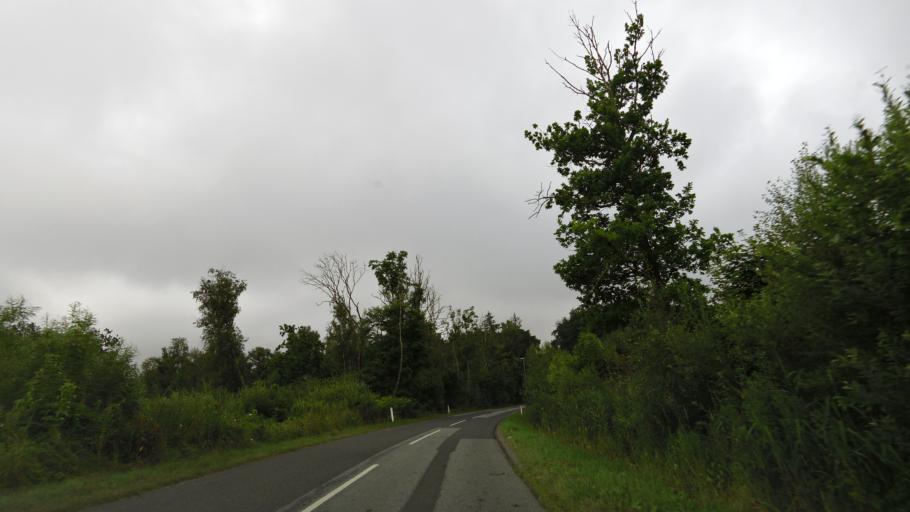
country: DK
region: South Denmark
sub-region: Nordfyns Kommune
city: Otterup
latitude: 55.5673
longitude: 10.3907
